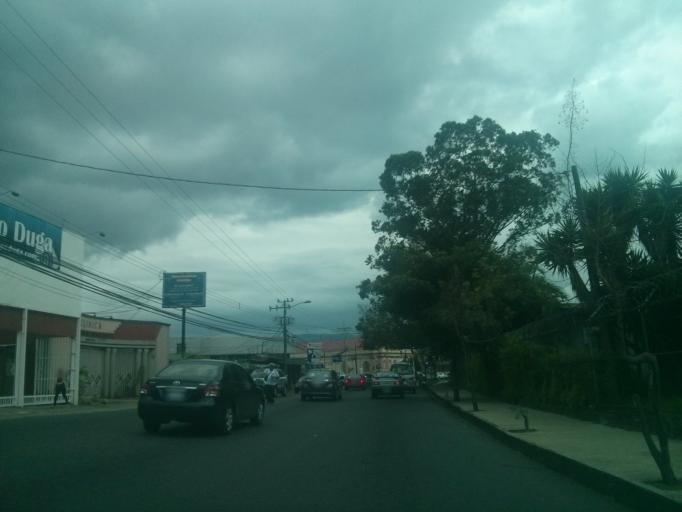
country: CR
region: San Jose
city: San Pedro
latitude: 9.9215
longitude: -84.0543
